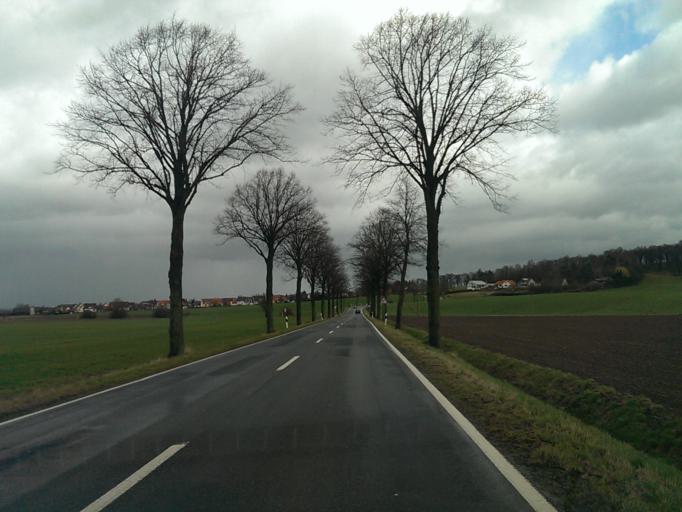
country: DE
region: Lower Saxony
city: Schellerten
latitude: 52.1422
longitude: 10.0752
